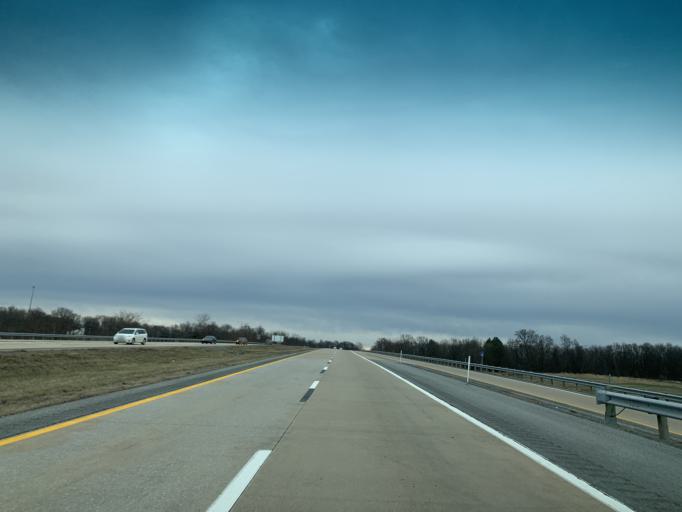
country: US
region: West Virginia
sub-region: Jefferson County
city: Ranson
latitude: 39.3793
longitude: -77.8926
